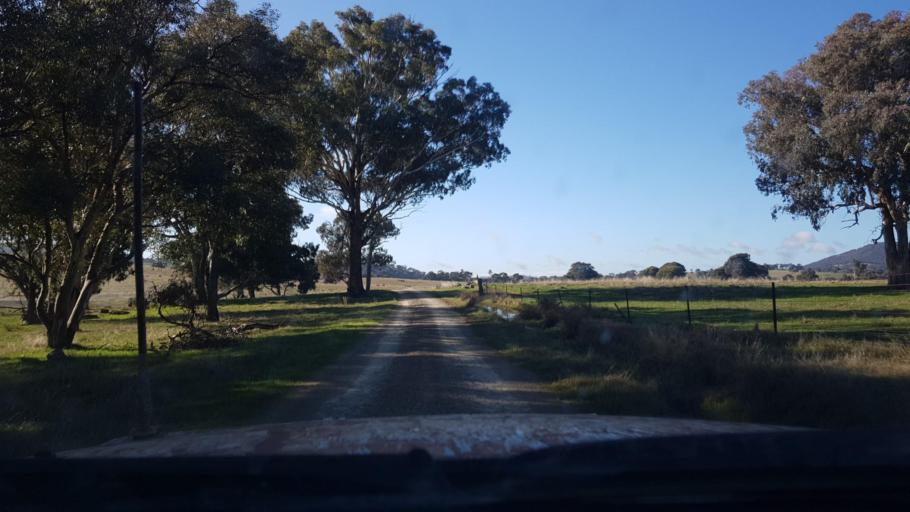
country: AU
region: New South Wales
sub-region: Gundagai
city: Gundagai
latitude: -34.8982
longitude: 147.9542
